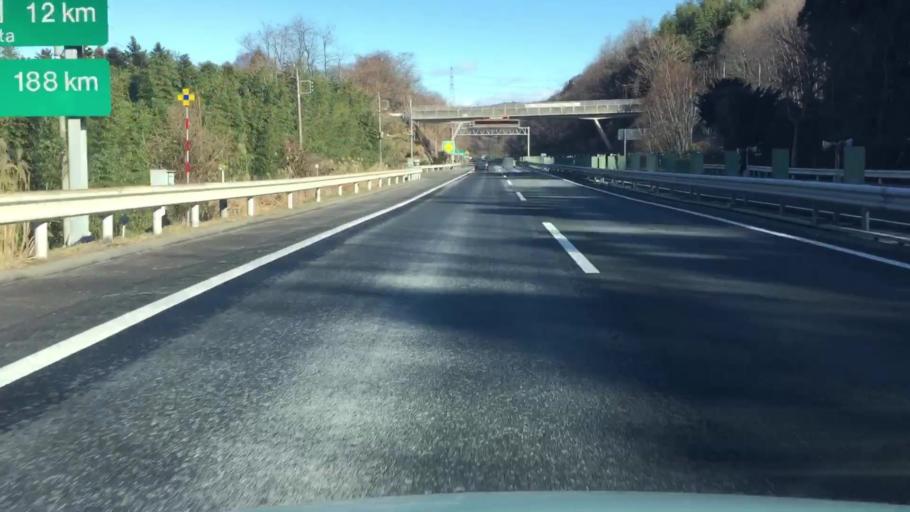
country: JP
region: Gunma
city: Numata
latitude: 36.5541
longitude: 139.0557
